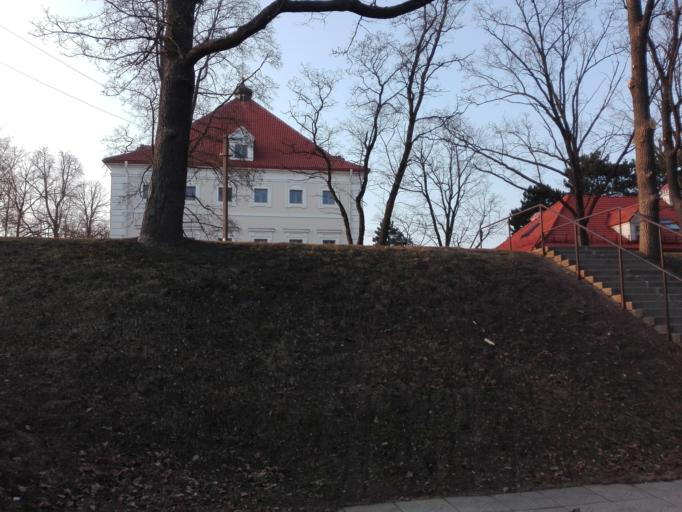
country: LT
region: Panevezys
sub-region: Birzai
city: Birzai
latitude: 56.2042
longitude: 24.7540
